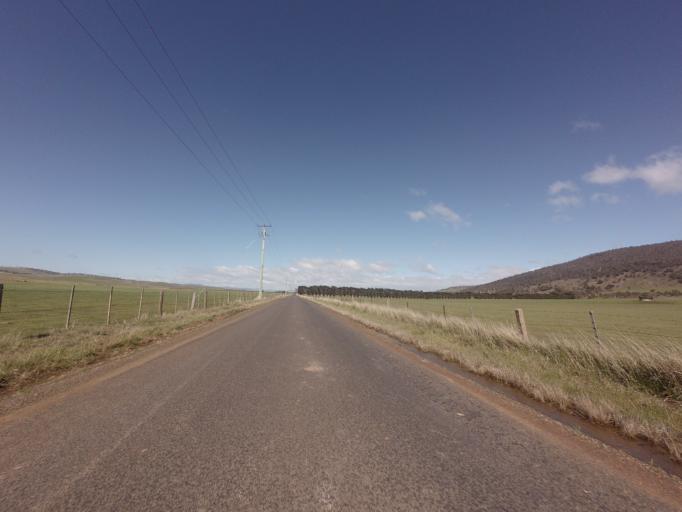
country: AU
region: Tasmania
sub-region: Northern Midlands
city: Evandale
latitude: -41.9633
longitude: 147.4396
